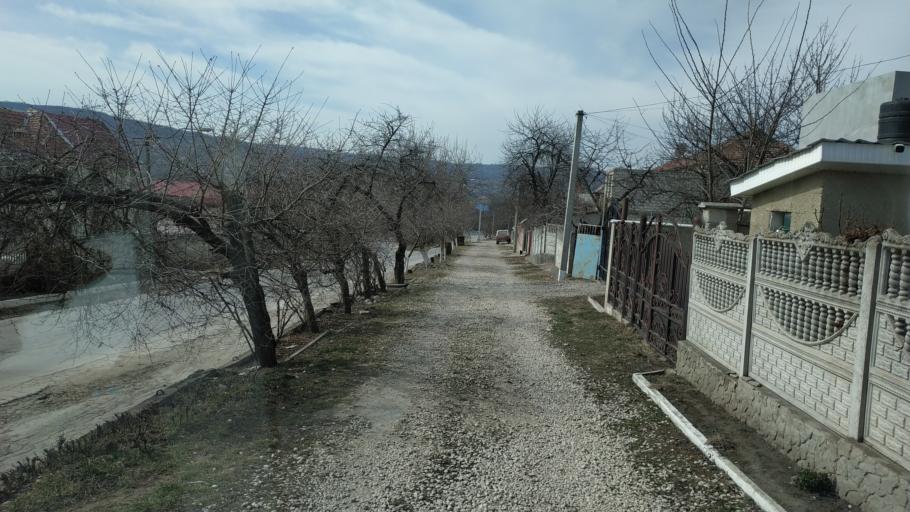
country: MD
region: Chisinau
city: Vatra
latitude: 47.0943
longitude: 28.6751
